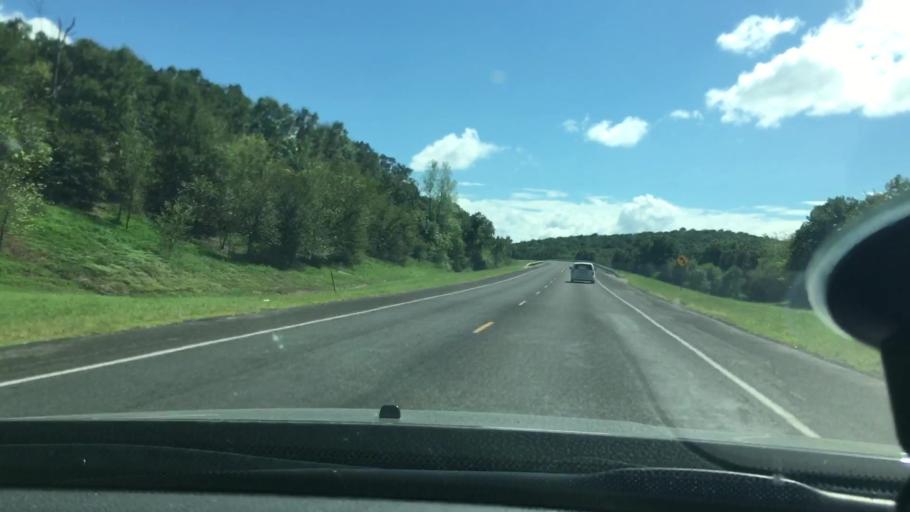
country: US
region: Oklahoma
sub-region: Sequoyah County
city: Vian
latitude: 35.5312
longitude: -94.9729
